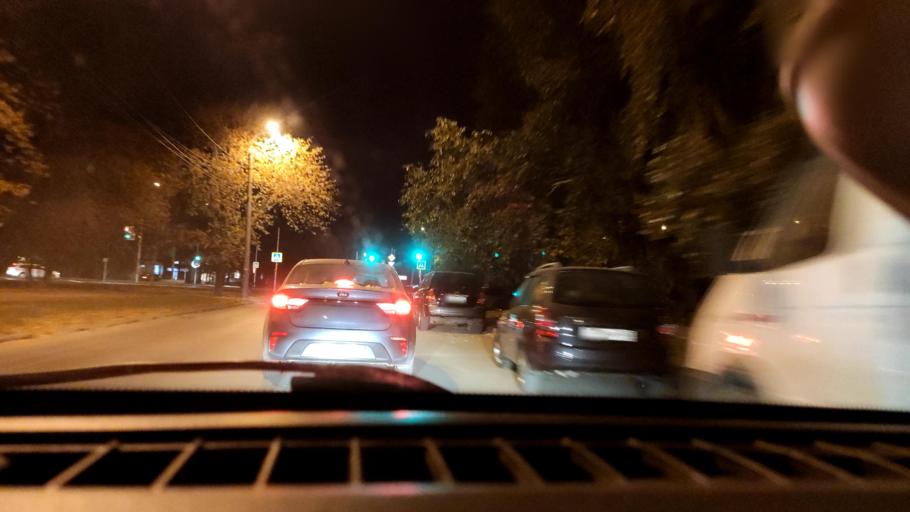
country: RU
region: Samara
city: Samara
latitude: 53.2145
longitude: 50.2102
